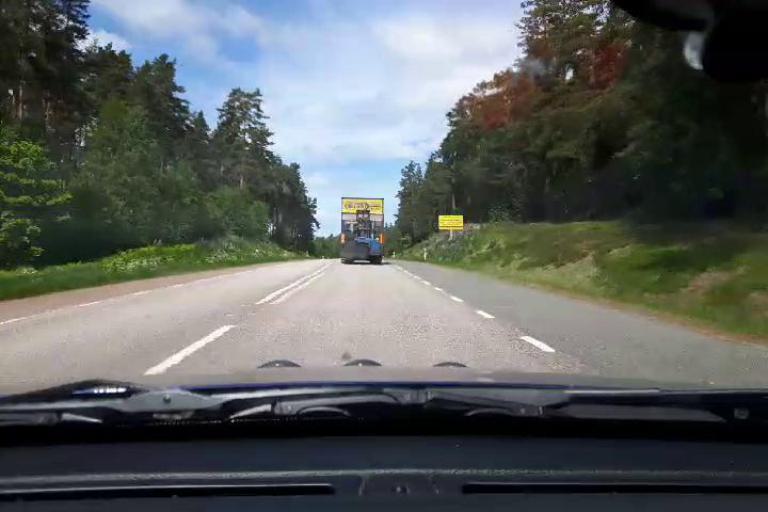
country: SE
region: Uppsala
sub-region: Osthammars Kommun
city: Bjorklinge
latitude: 60.0929
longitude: 17.5545
